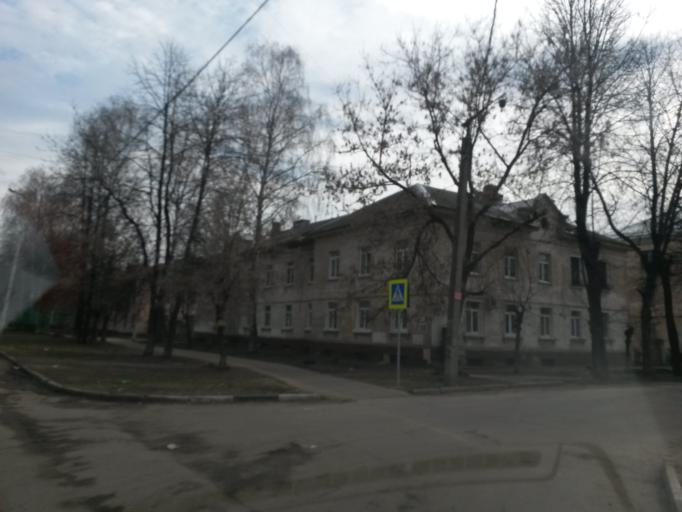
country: RU
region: Jaroslavl
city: Yaroslavl
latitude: 57.6343
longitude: 39.8359
